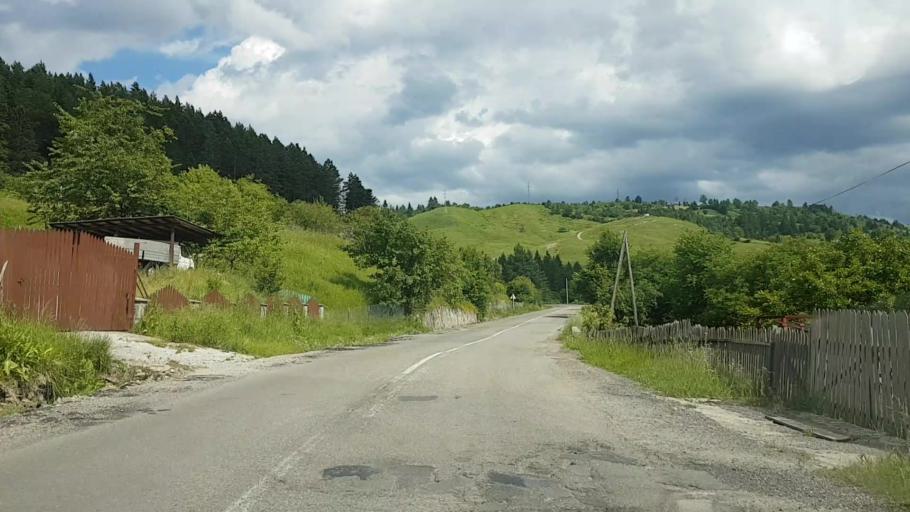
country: RO
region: Neamt
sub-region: Comuna Hangu
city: Hangu
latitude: 47.0071
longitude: 26.0920
